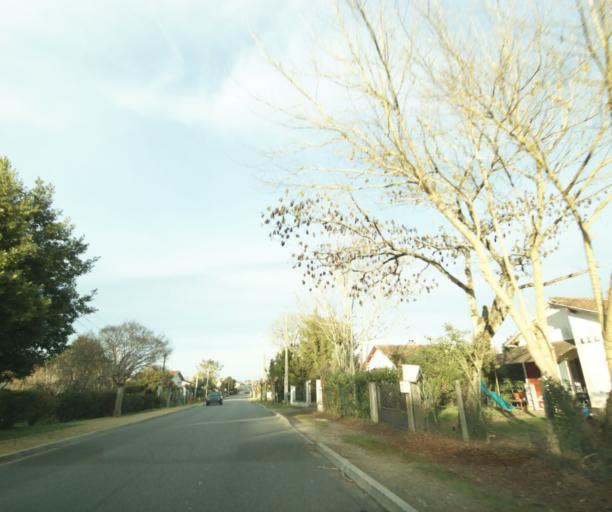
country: FR
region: Aquitaine
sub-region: Departement des Landes
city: Gabarret
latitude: 43.9806
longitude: 0.0081
